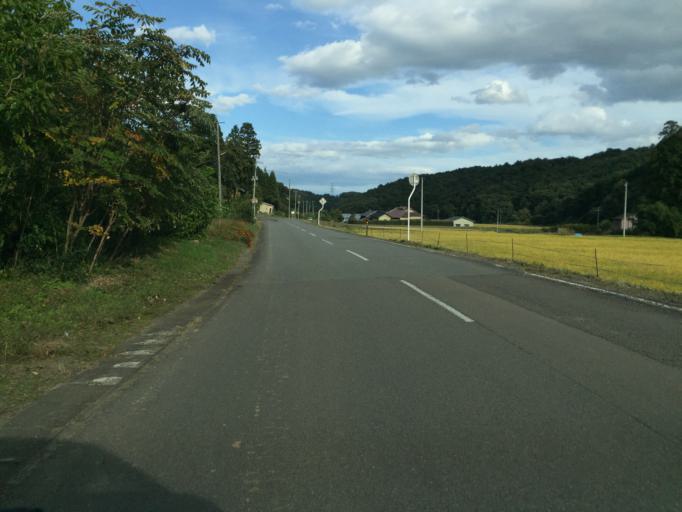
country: JP
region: Fukushima
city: Nihommatsu
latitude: 37.6717
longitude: 140.3973
